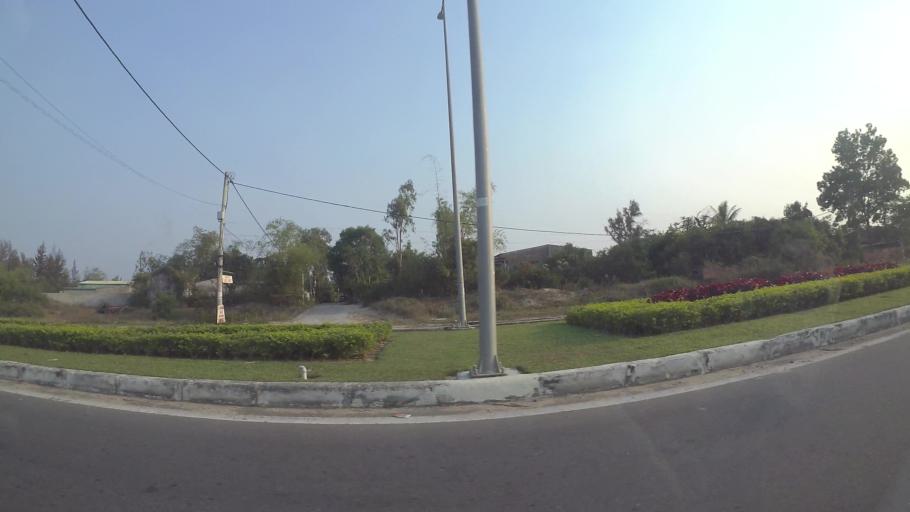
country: VN
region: Da Nang
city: Ngu Hanh Son
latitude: 15.9776
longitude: 108.2368
